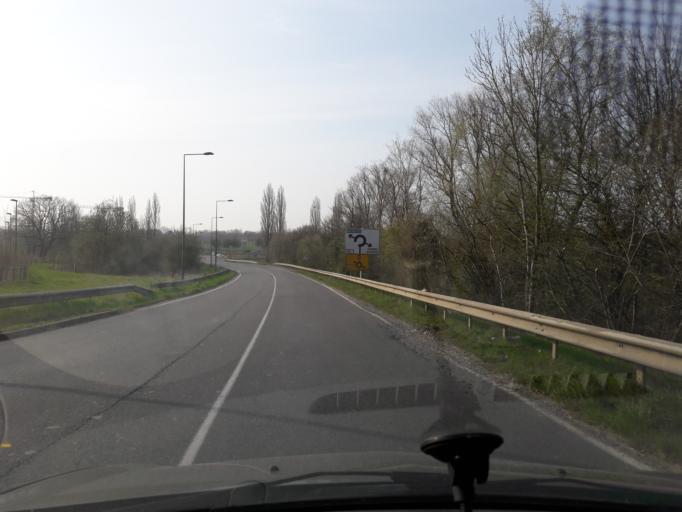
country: FR
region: Nord-Pas-de-Calais
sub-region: Departement du Nord
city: Rousies
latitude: 50.2786
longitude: 3.9984
